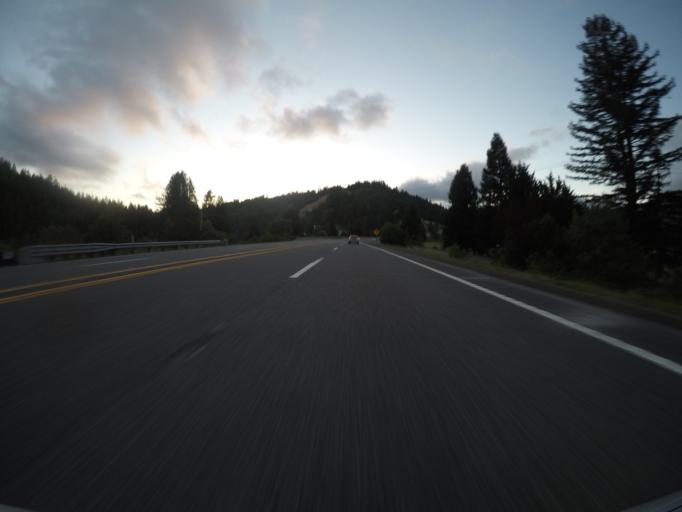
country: US
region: California
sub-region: Humboldt County
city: Redway
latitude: 40.0655
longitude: -123.7862
